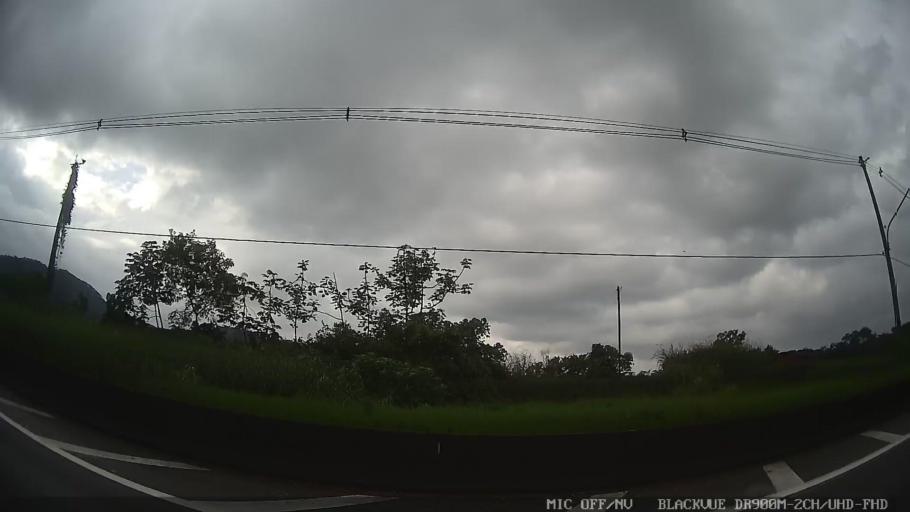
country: BR
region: Sao Paulo
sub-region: Cubatao
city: Cubatao
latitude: -23.8707
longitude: -46.4212
